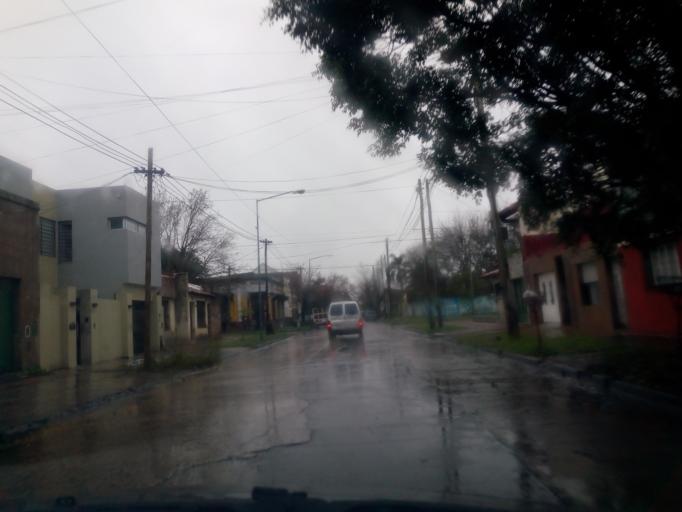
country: AR
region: Buenos Aires
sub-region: Partido de Lanus
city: Lanus
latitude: -34.7261
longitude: -58.3875
